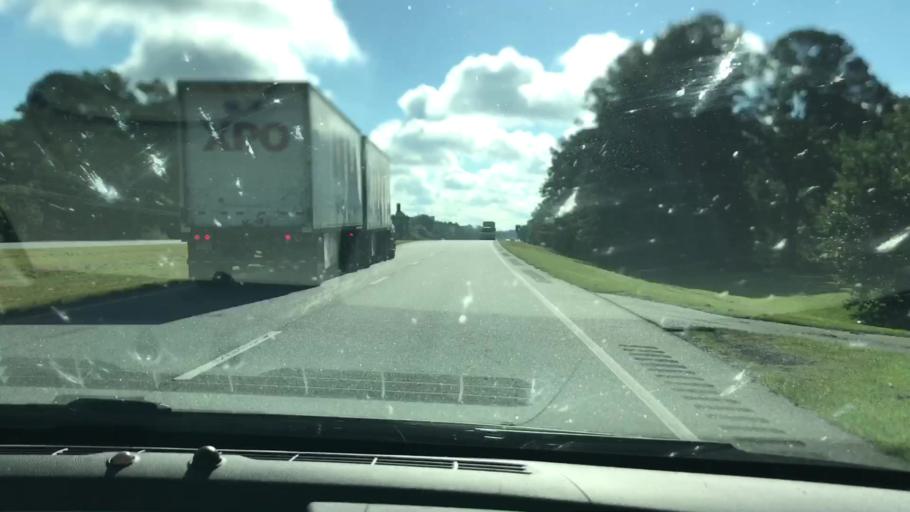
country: US
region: Georgia
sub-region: Dougherty County
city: Putney
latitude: 31.5545
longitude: -83.9892
